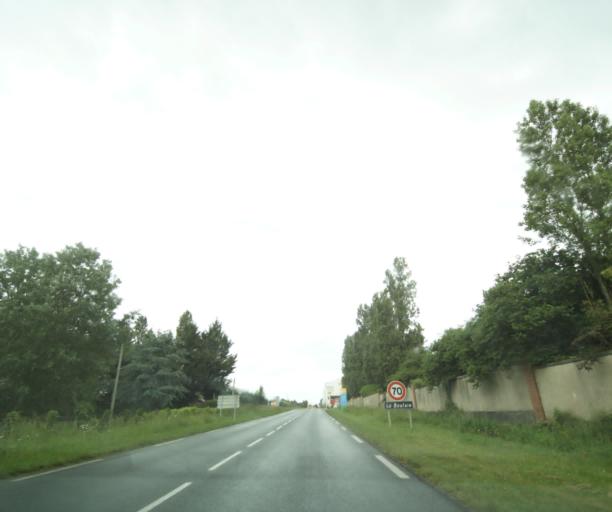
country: FR
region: Poitou-Charentes
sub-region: Departement des Deux-Sevres
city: Chatillon-sur-Thouet
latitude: 46.6674
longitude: -0.2469
